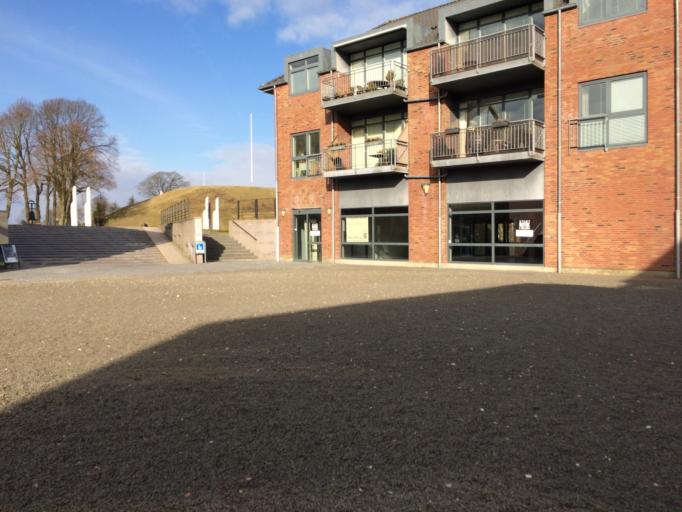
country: DK
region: South Denmark
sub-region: Vejle Kommune
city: Jelling
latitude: 55.7550
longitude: 9.4182
